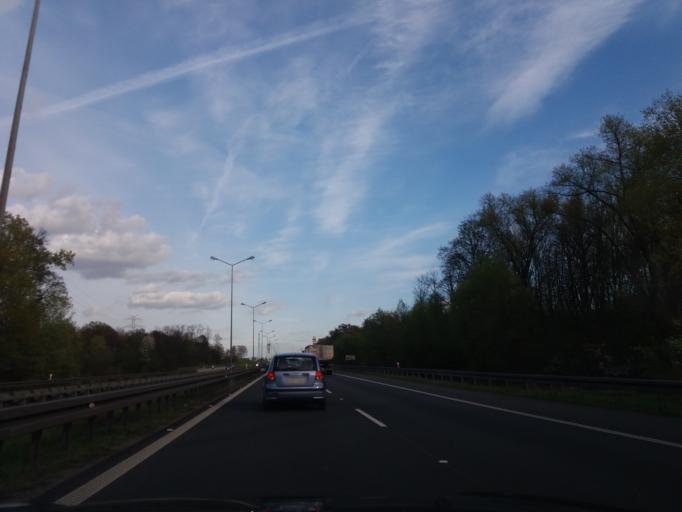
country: PL
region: Lower Silesian Voivodeship
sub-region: Powiat strzelinski
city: Wiazow
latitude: 50.8485
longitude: 17.2423
